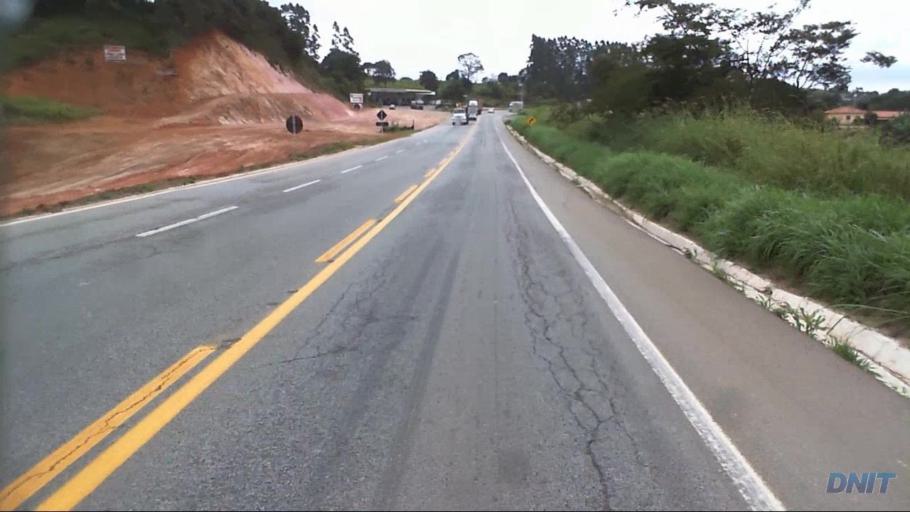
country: BR
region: Minas Gerais
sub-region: Caete
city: Caete
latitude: -19.7423
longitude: -43.5533
